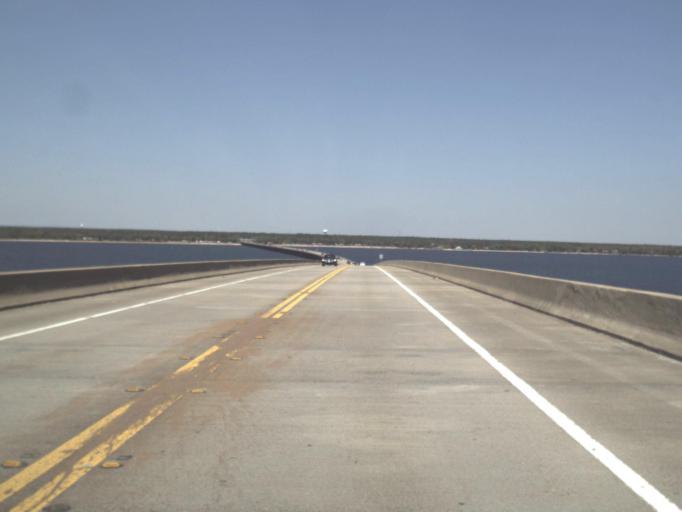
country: US
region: Florida
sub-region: Walton County
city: Miramar Beach
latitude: 30.4344
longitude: -86.4177
